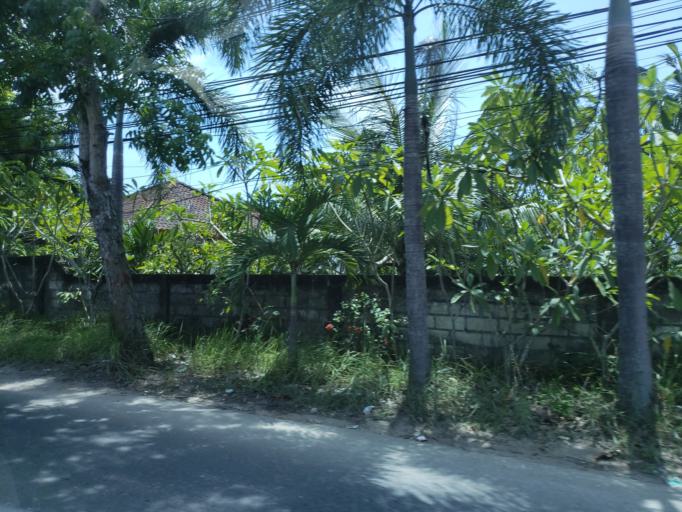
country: ID
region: Bali
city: Kangin
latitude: -8.8209
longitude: 115.1470
